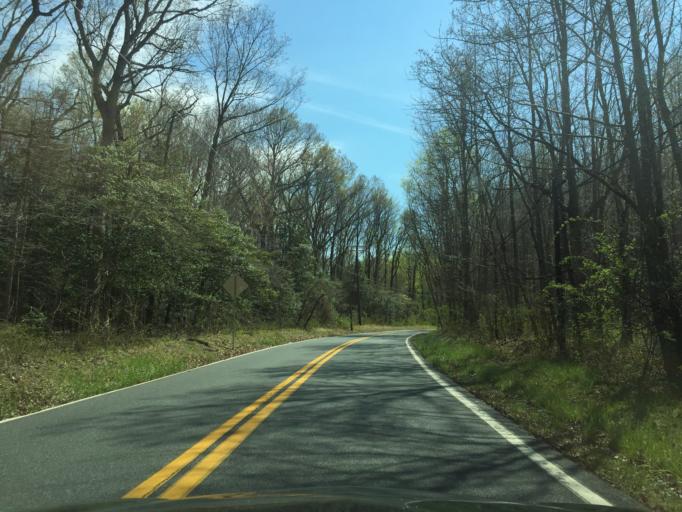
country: US
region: Maryland
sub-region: Baltimore County
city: Edgemere
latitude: 39.2598
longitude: -76.4172
